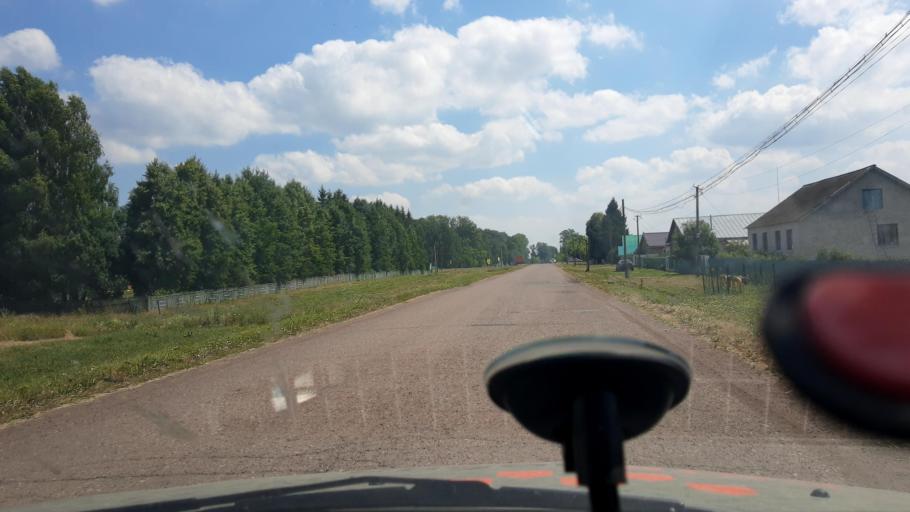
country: RU
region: Bashkortostan
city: Chekmagush
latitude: 54.8779
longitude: 54.6098
